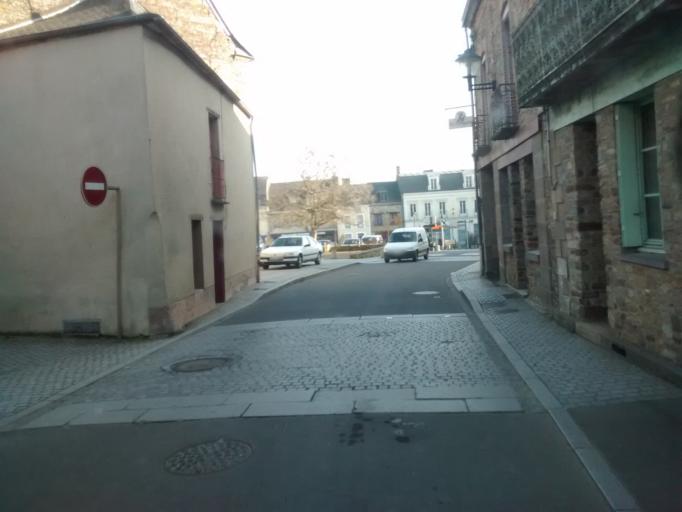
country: FR
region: Brittany
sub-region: Departement d'Ille-et-Vilaine
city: Grand-Fougeray
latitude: 47.7238
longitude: -1.7326
